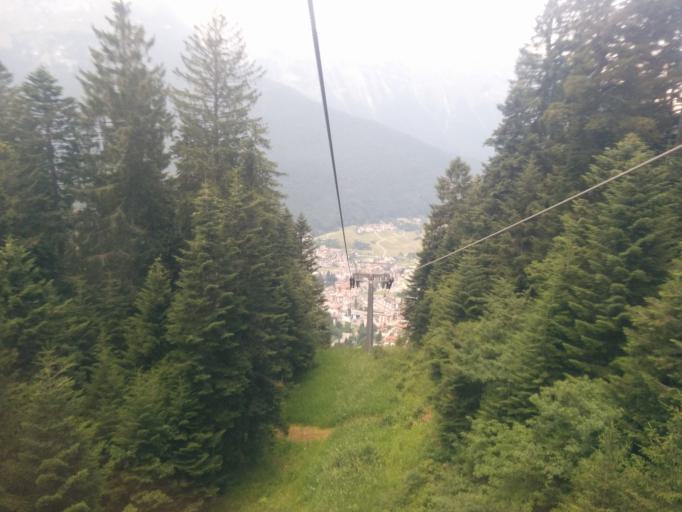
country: IT
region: Trentino-Alto Adige
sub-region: Provincia di Trento
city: Andalo
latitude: 46.1555
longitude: 11.0127
